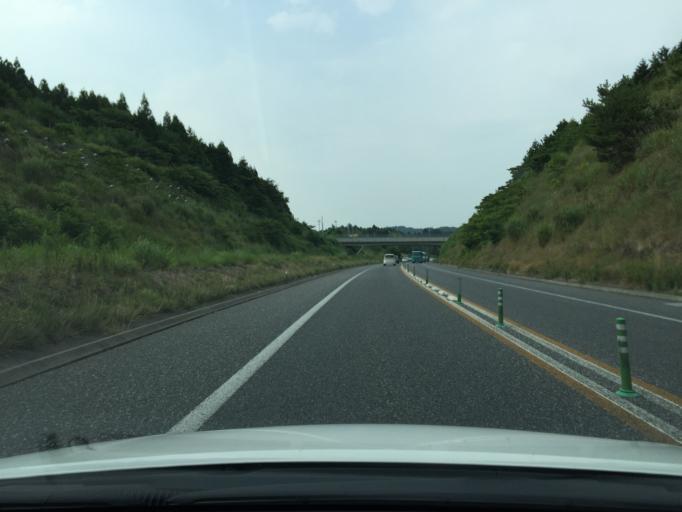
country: JP
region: Fukushima
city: Iwaki
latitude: 37.2219
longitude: 140.9767
